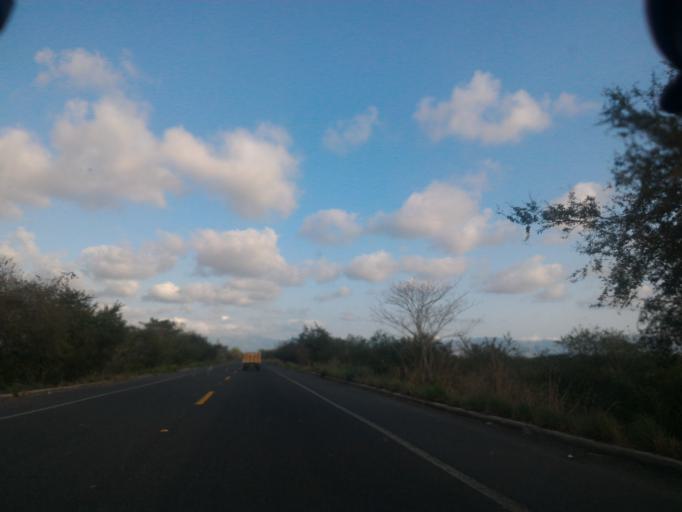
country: MX
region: Michoacan
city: Coahuayana Viejo
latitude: 18.7803
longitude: -103.7636
